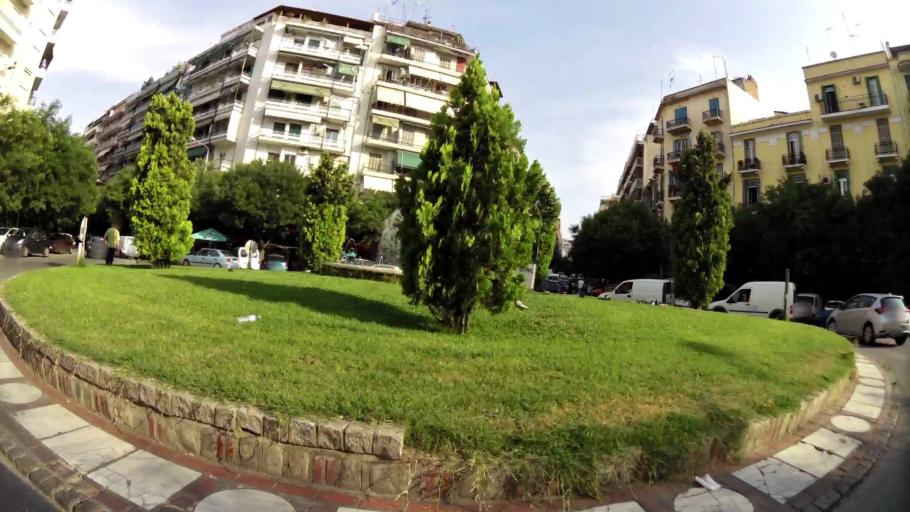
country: GR
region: Central Macedonia
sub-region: Nomos Thessalonikis
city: Thessaloniki
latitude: 40.6403
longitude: 22.9404
